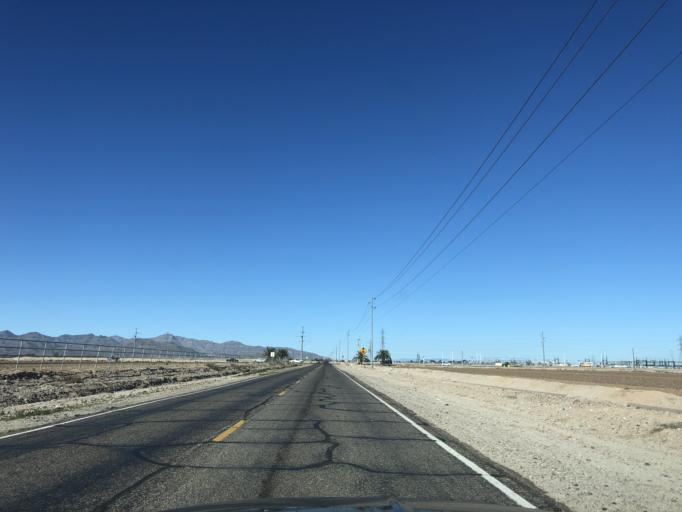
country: US
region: Arizona
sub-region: Maricopa County
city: Buckeye
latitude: 33.4041
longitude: -112.5042
